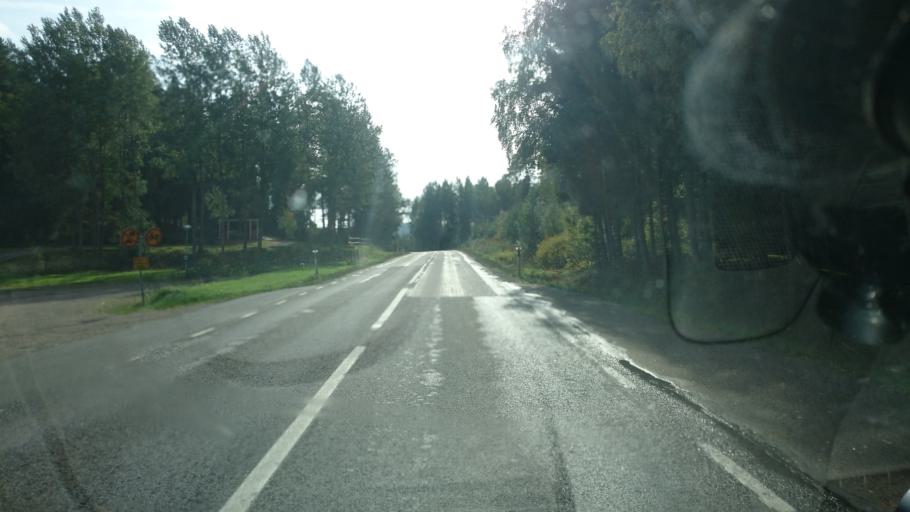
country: SE
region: Vaestra Goetaland
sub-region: Alingsas Kommun
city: Sollebrunn
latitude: 58.1278
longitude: 12.4983
